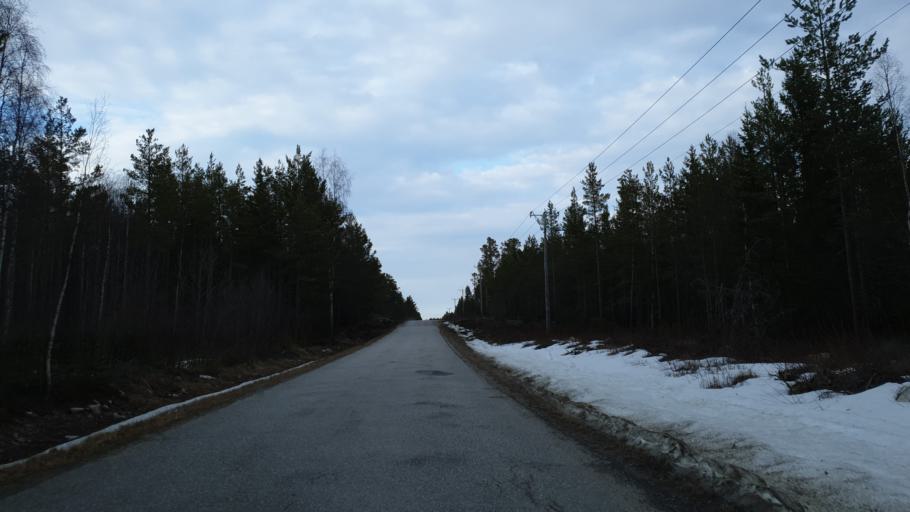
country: SE
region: Vaesternorrland
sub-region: Sundsvalls Kommun
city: Njurundabommen
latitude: 61.9900
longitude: 17.3774
